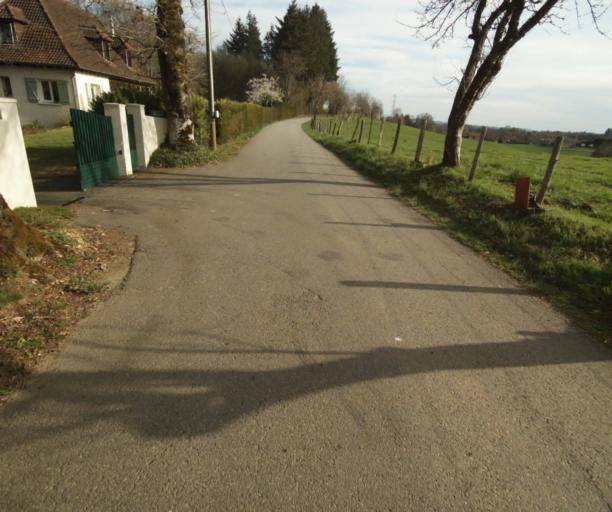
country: FR
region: Limousin
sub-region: Departement de la Correze
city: Naves
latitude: 45.3185
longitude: 1.7466
